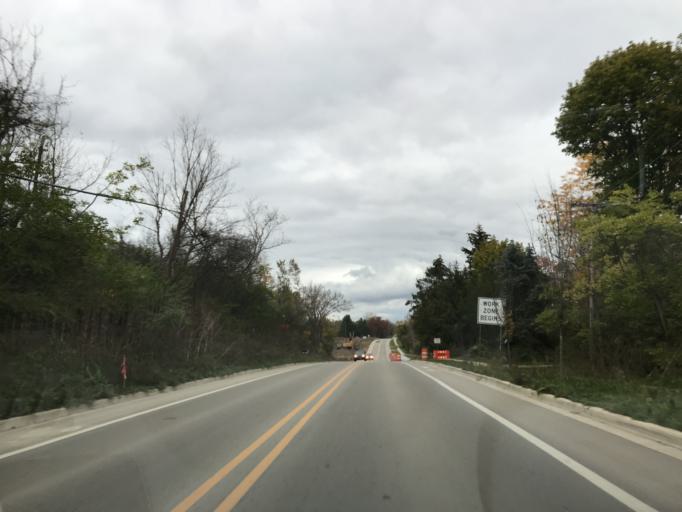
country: US
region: Michigan
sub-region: Washtenaw County
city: Ann Arbor
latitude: 42.3093
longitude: -83.7349
